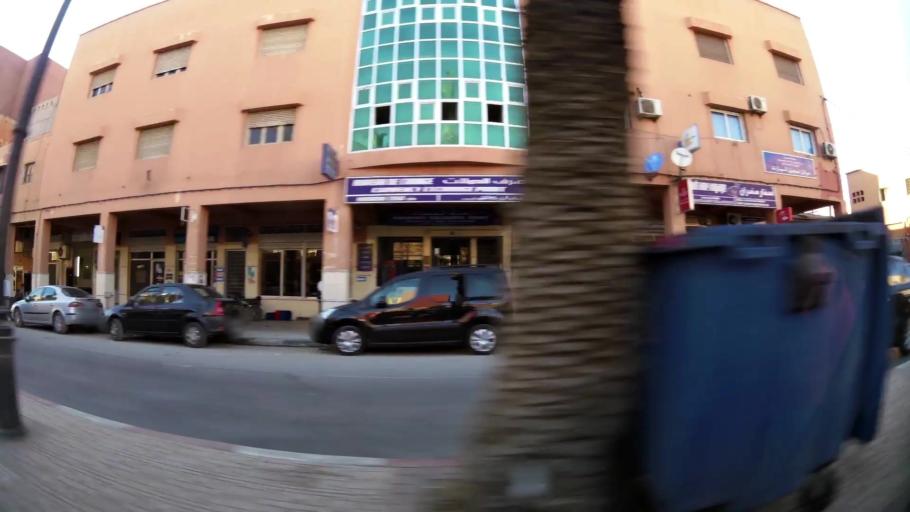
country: MA
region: Oriental
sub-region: Berkane-Taourirt
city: Berkane
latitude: 34.9240
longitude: -2.3354
